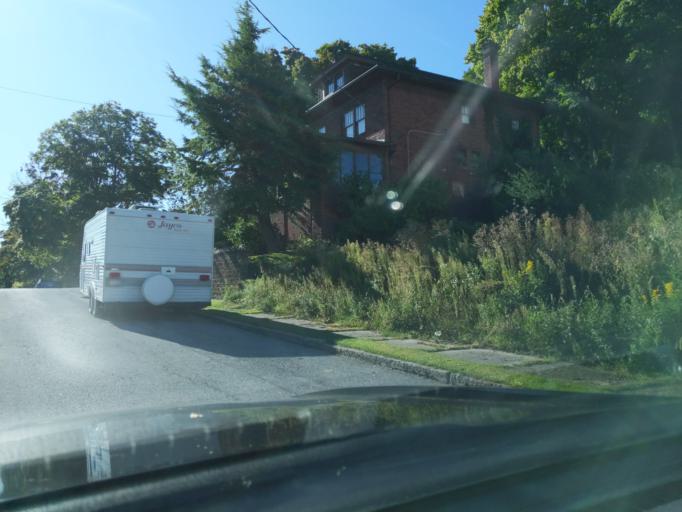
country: US
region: Pennsylvania
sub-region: Blair County
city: Altoona
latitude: 40.5249
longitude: -78.4024
